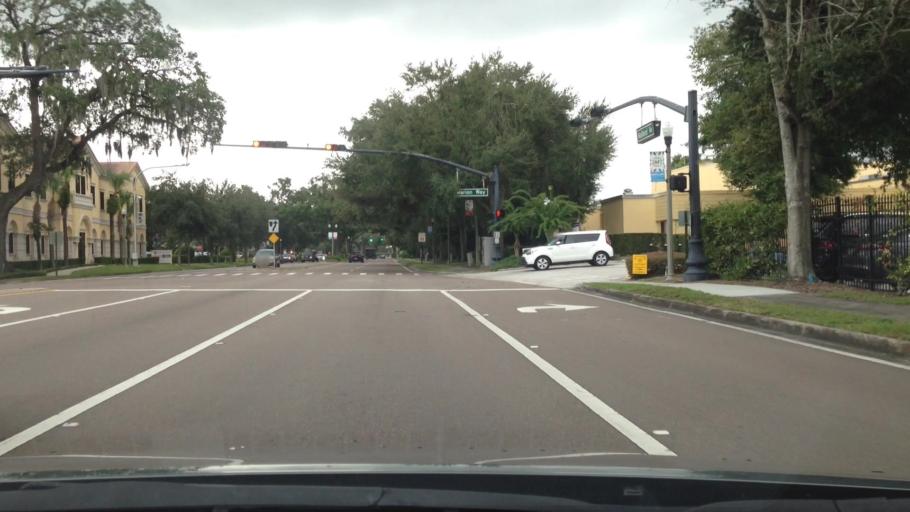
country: US
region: Florida
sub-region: Orange County
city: Maitland
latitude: 28.6352
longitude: -81.3658
